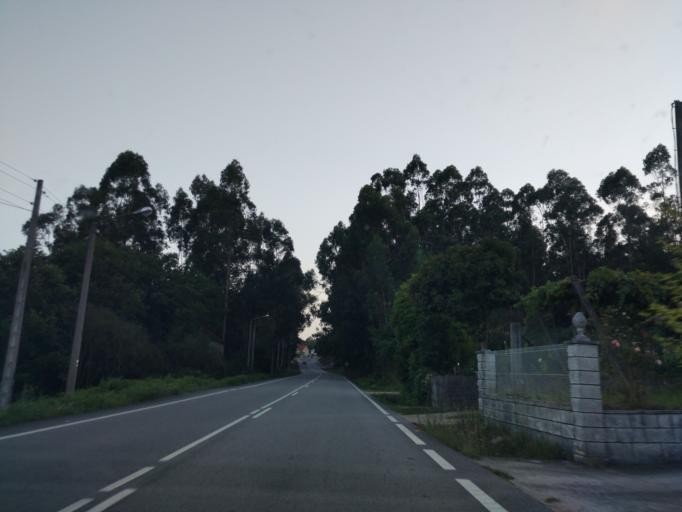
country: ES
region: Galicia
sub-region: Provincia da Coruna
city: Padron
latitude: 42.7238
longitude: -8.6784
